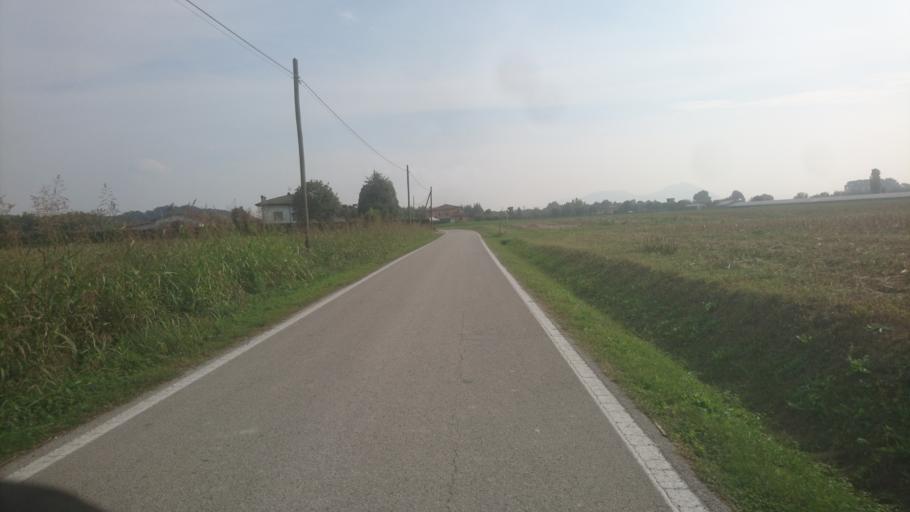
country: IT
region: Veneto
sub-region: Provincia di Vicenza
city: Montegalda
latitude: 45.4617
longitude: 11.6552
